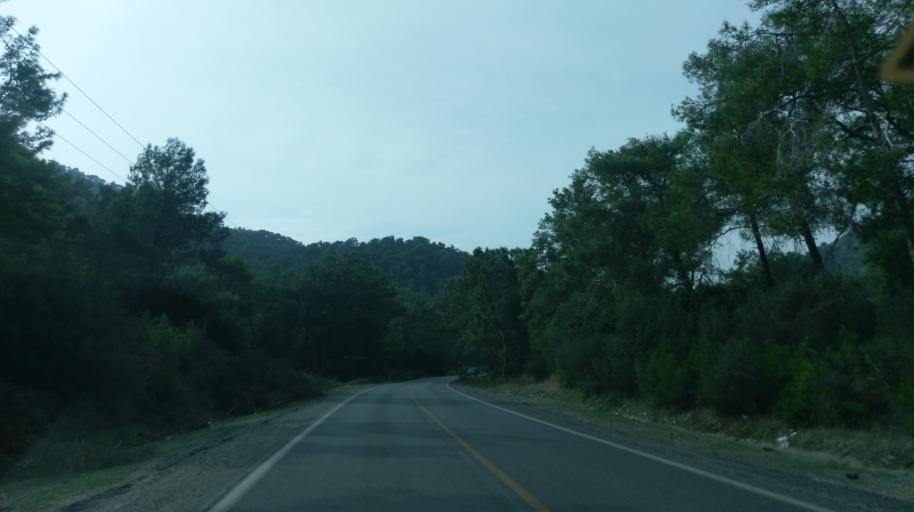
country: CY
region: Keryneia
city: Lapithos
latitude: 35.3448
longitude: 33.0801
